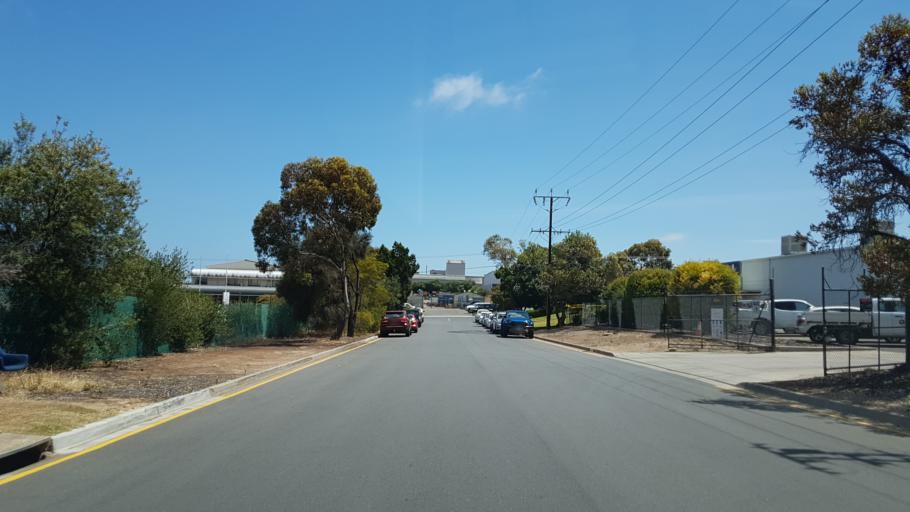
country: AU
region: South Australia
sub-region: Onkaparinga
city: Morphett Vale
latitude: -35.1143
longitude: 138.5009
